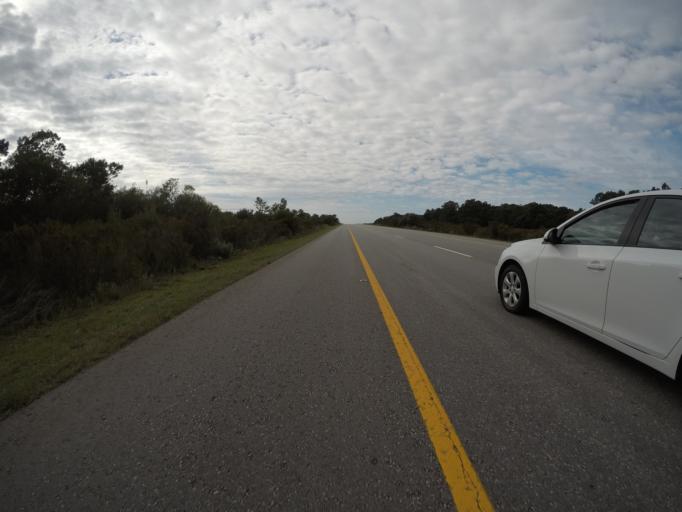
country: ZA
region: Eastern Cape
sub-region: Cacadu District Municipality
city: Kruisfontein
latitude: -33.9974
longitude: 24.7469
